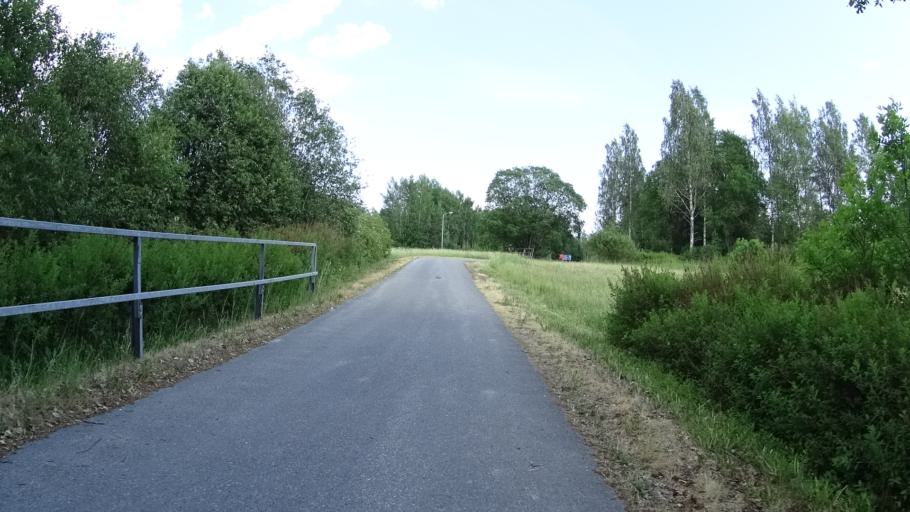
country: FI
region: Uusimaa
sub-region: Raaseporin
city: Karis
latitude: 60.0947
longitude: 23.6273
